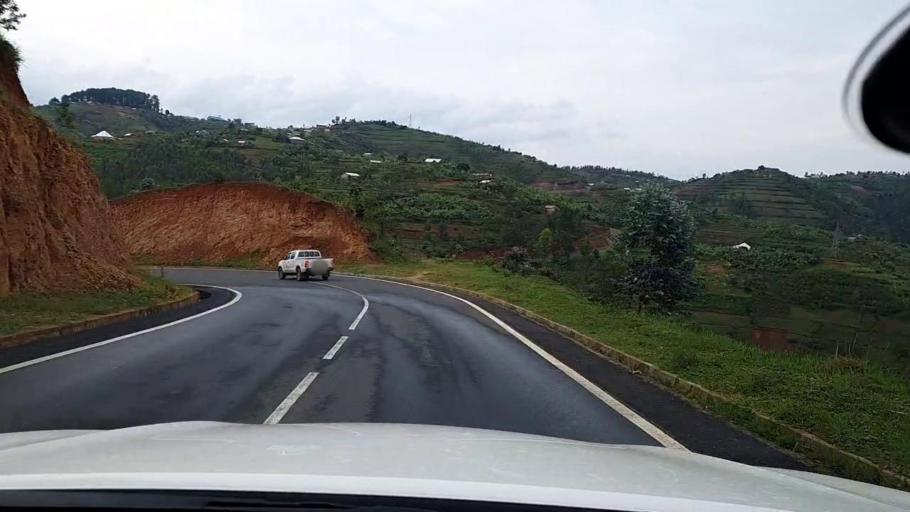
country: RW
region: Western Province
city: Kibuye
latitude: -2.1628
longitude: 29.2955
